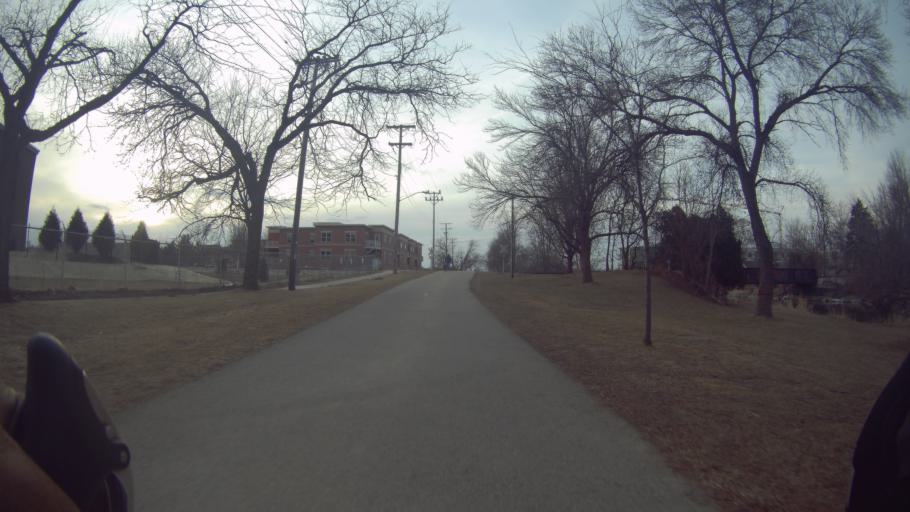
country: US
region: Wisconsin
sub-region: Dane County
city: Maple Bluff
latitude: 43.0885
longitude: -89.3598
